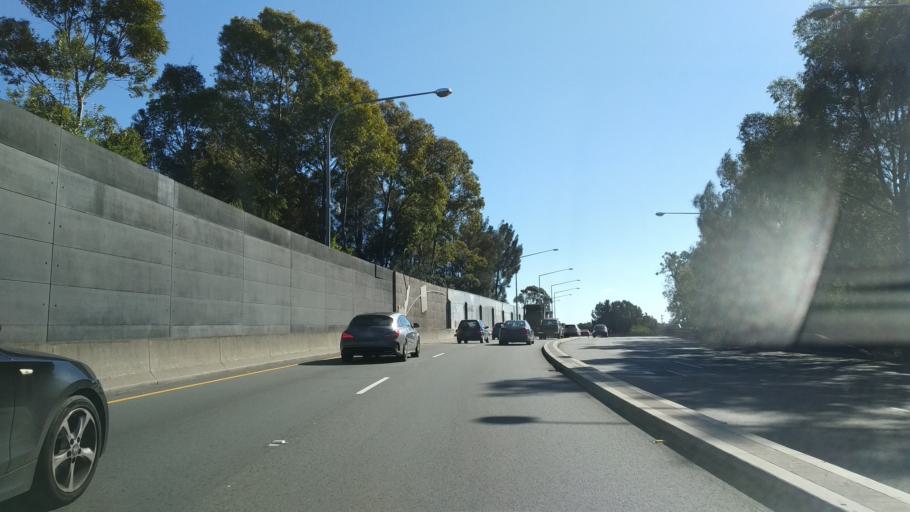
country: AU
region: New South Wales
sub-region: Leichhardt
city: Leichhardt
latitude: -33.8739
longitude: 151.1506
